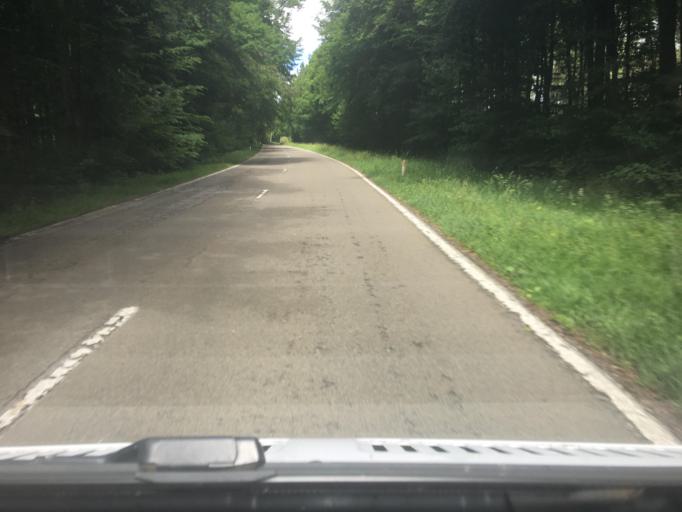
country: BE
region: Wallonia
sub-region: Province du Luxembourg
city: Florenville
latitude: 49.6457
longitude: 5.3413
